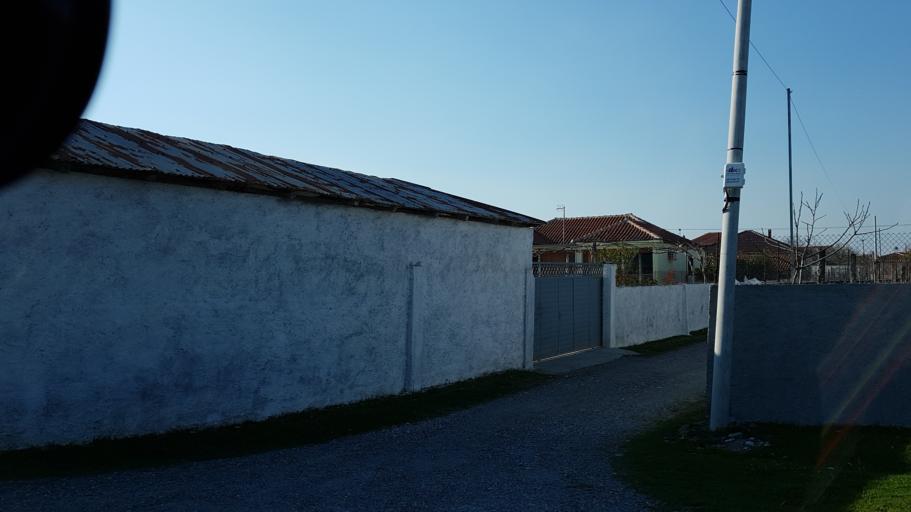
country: AL
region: Shkoder
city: Vukatane
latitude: 41.9904
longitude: 19.5541
